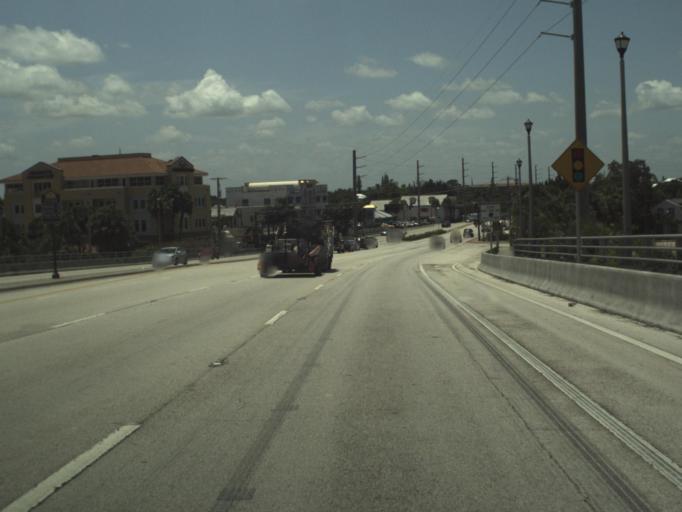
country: US
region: Florida
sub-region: Martin County
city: Stuart
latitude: 27.2007
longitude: -80.2576
